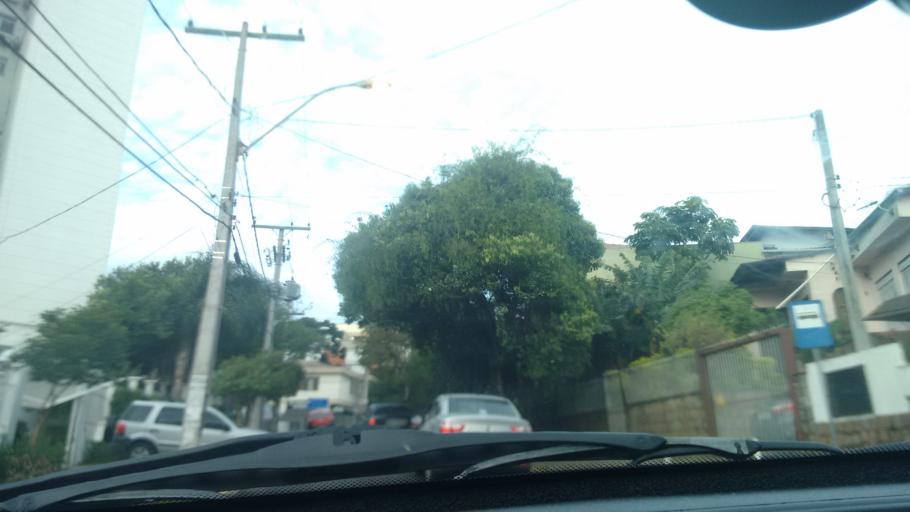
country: BR
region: Rio Grande do Sul
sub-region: Porto Alegre
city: Porto Alegre
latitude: -30.0082
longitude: -51.1560
